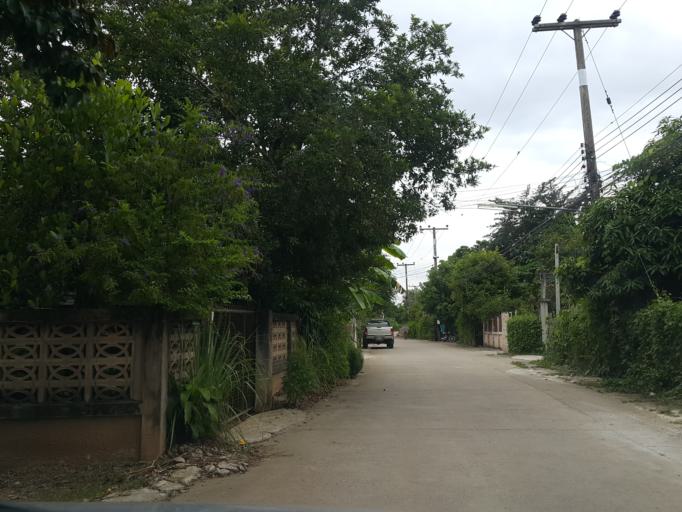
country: TH
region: Chiang Mai
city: San Sai
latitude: 18.8271
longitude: 99.1242
